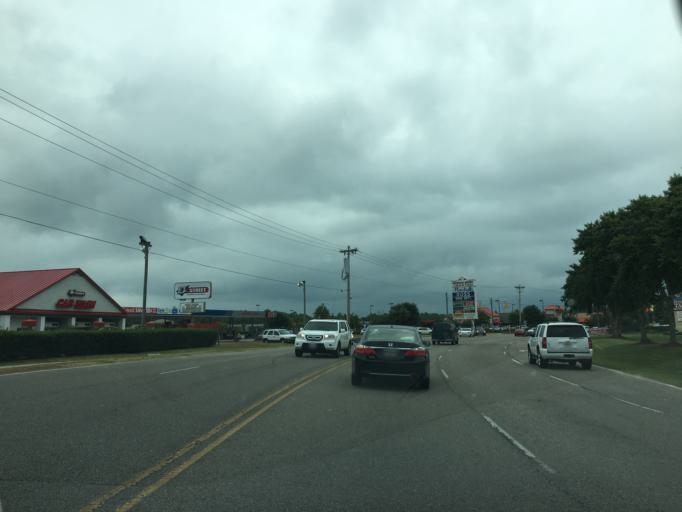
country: US
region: South Carolina
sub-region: Horry County
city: North Myrtle Beach
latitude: 33.7859
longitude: -78.7712
